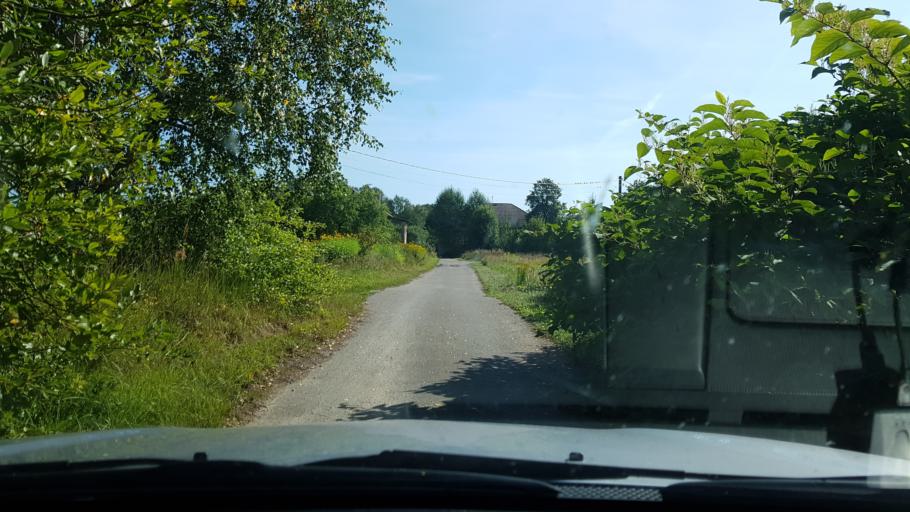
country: EE
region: Ida-Virumaa
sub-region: Sillamaee linn
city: Sillamae
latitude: 59.3383
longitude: 27.6797
